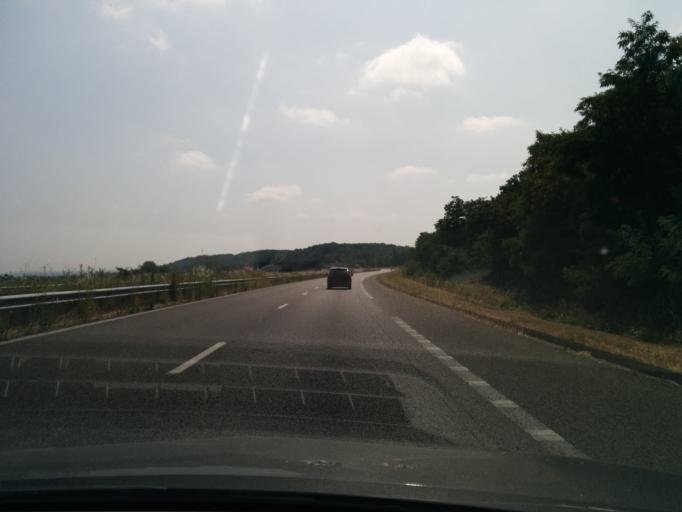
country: FR
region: Midi-Pyrenees
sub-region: Departement de la Haute-Garonne
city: Buzet-sur-Tarn
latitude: 43.7477
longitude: 1.6231
